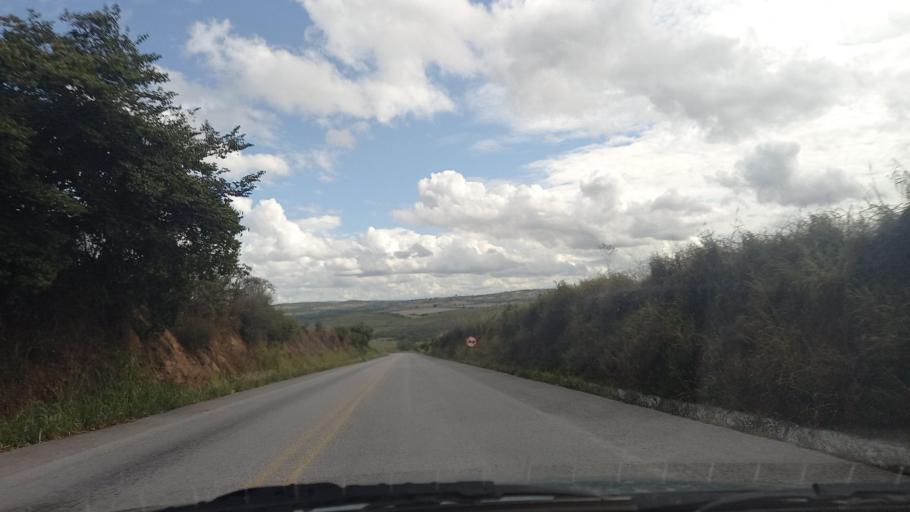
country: BR
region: Pernambuco
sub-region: Lajedo
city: Lajedo
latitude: -8.7243
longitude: -36.4292
